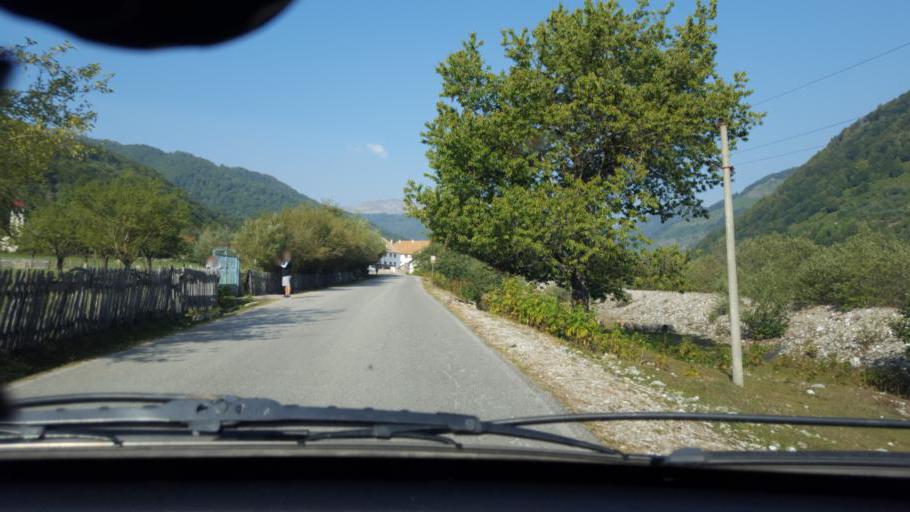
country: ME
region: Andrijevica
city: Andrijevica
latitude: 42.5895
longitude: 19.6958
